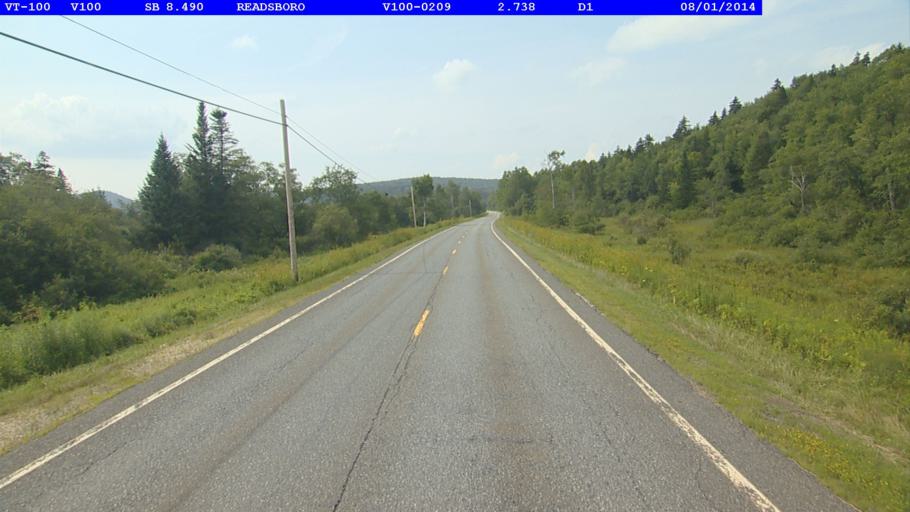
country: US
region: Massachusetts
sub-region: Berkshire County
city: North Adams
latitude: 42.8224
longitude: -72.9815
